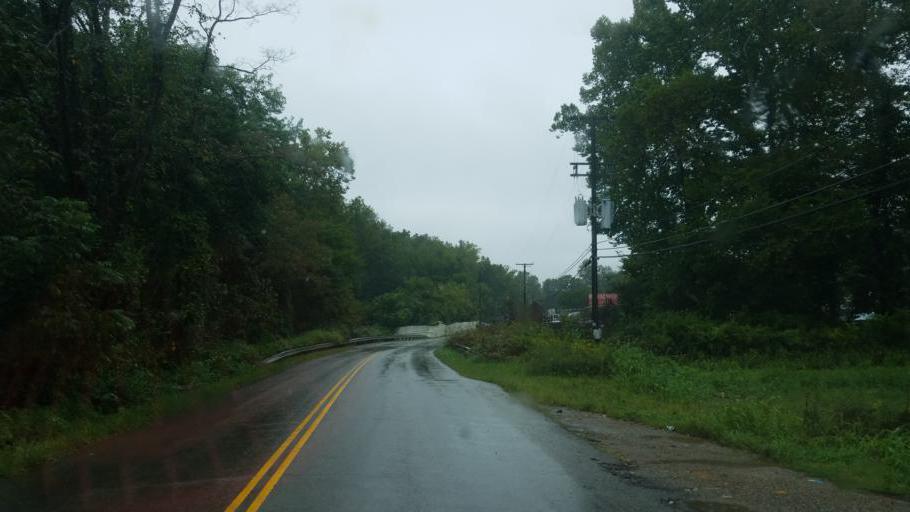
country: US
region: Ohio
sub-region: Scioto County
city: West Portsmouth
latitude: 38.7238
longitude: -83.0471
